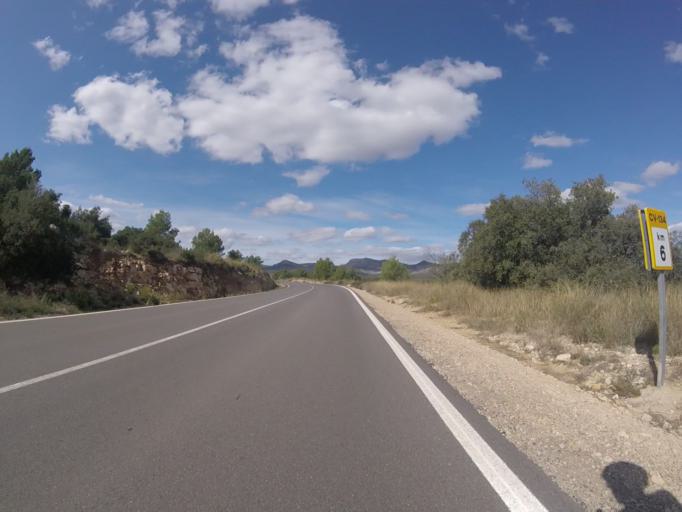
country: ES
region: Valencia
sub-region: Provincia de Castello
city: Chert/Xert
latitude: 40.4390
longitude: 0.1127
